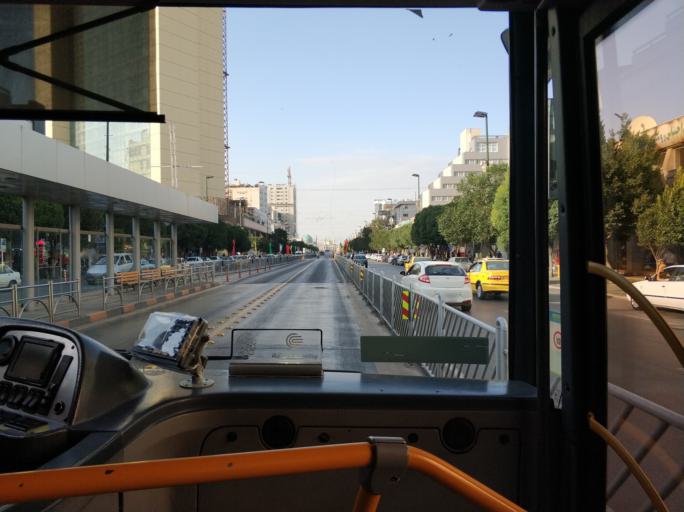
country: IR
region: Razavi Khorasan
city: Mashhad
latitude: 36.2794
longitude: 59.6085
